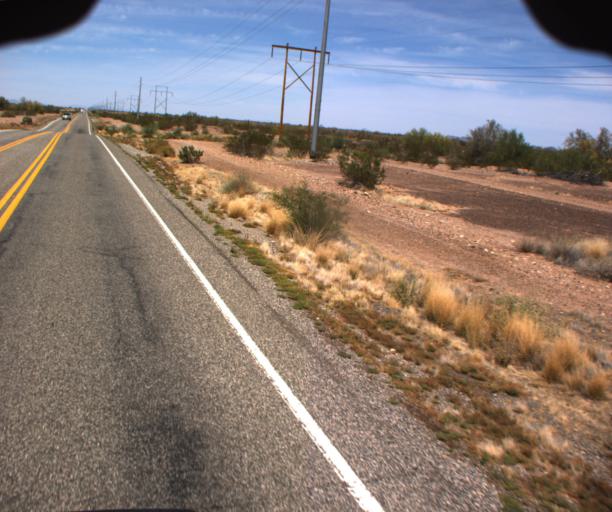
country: US
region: Arizona
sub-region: La Paz County
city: Quartzsite
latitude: 33.7511
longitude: -114.2170
